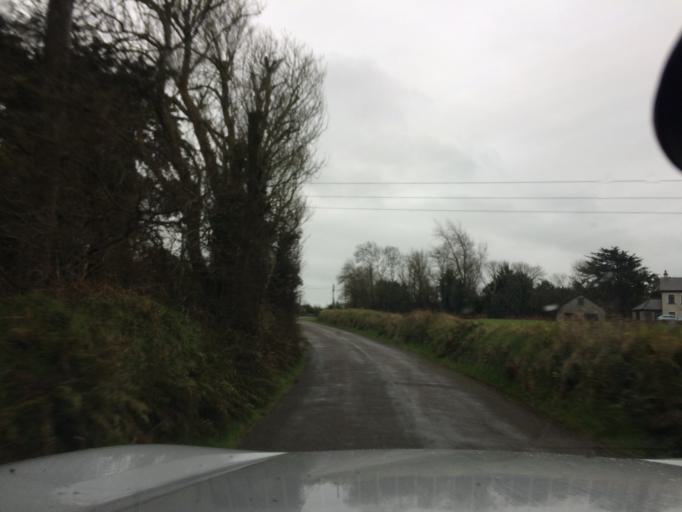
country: IE
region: Leinster
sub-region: Kilkenny
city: Mooncoin
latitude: 52.2327
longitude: -7.1918
